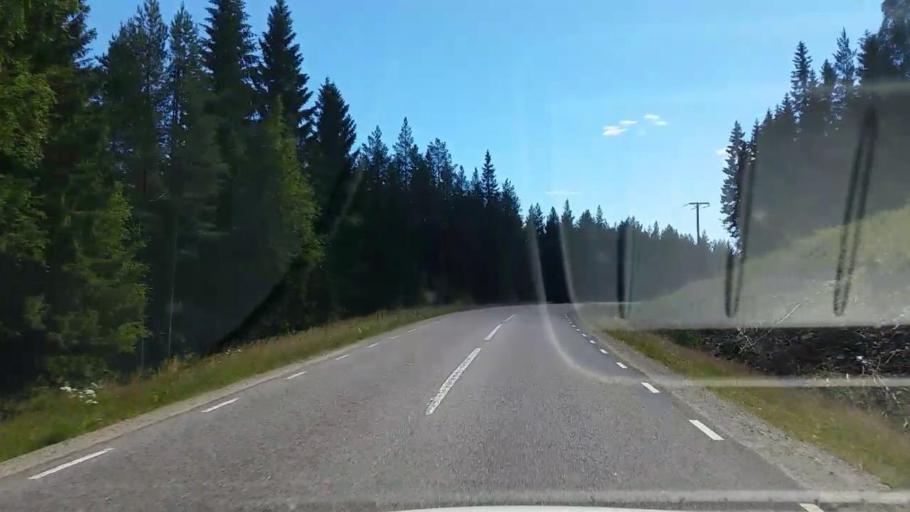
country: SE
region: Gaevleborg
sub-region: Ovanakers Kommun
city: Edsbyn
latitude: 61.5277
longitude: 15.6798
